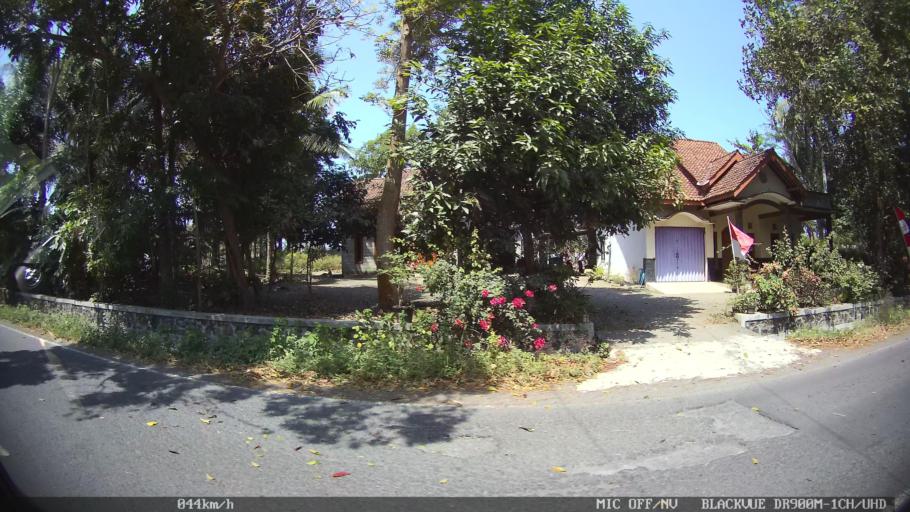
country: ID
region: Daerah Istimewa Yogyakarta
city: Srandakan
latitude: -7.9147
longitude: 110.0975
